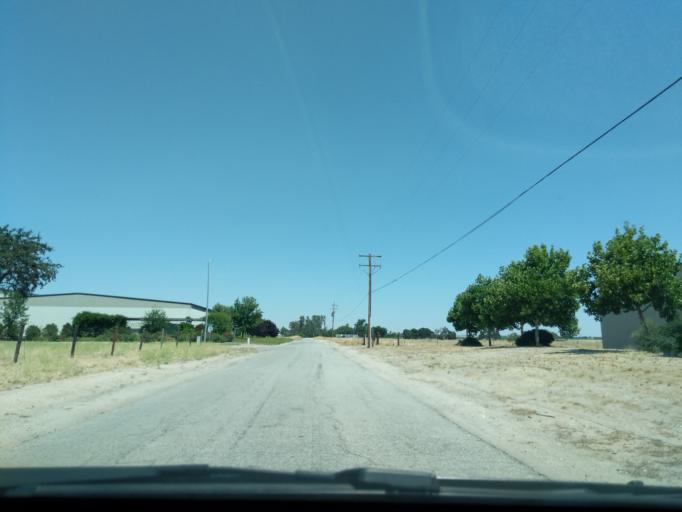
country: US
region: California
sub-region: San Luis Obispo County
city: Paso Robles
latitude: 35.6630
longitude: -120.6282
